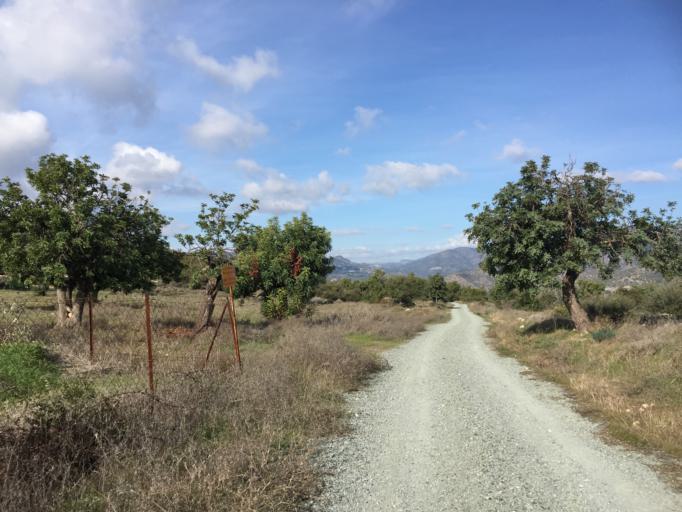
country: CY
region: Larnaka
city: Agios Tychon
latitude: 34.7476
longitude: 33.1254
